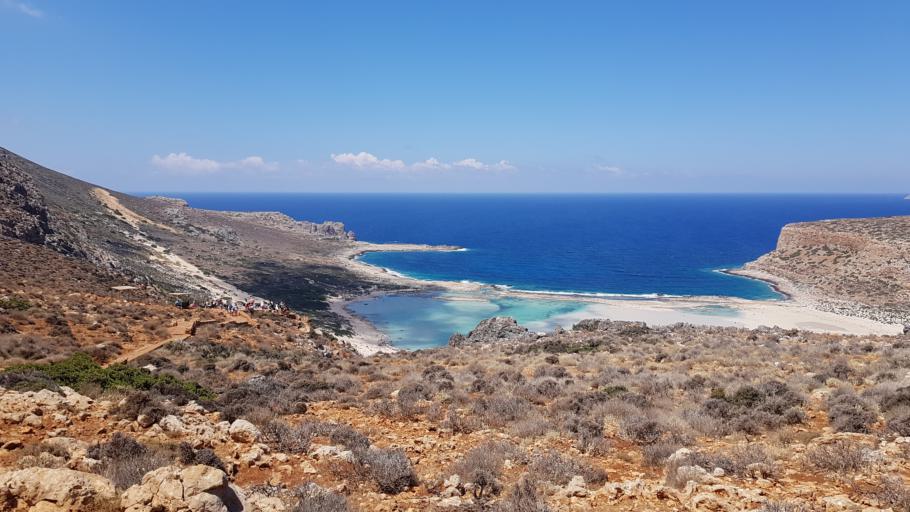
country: GR
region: Crete
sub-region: Nomos Chanias
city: Kissamos
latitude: 35.5845
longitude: 23.5958
